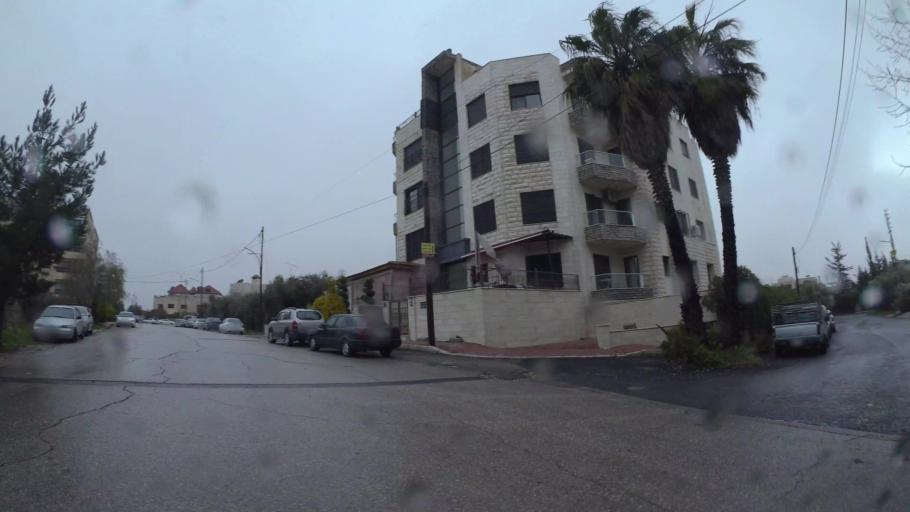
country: JO
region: Amman
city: Al Jubayhah
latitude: 32.0287
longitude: 35.8532
